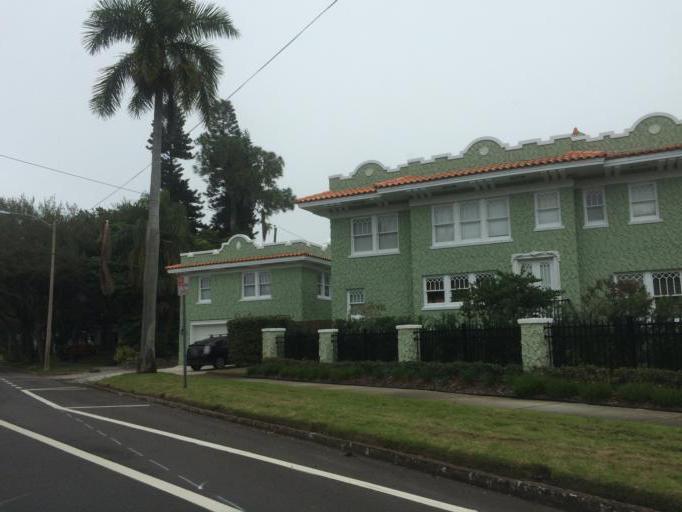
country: US
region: Florida
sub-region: Pinellas County
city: Saint Petersburg
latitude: 27.7849
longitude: -82.6267
